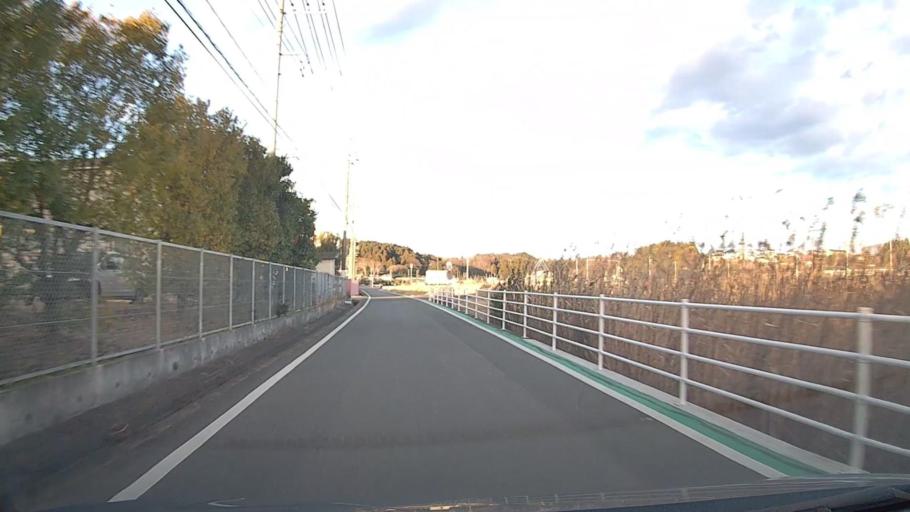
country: JP
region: Ibaraki
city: Kitaibaraki
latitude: 36.8492
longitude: 140.7754
